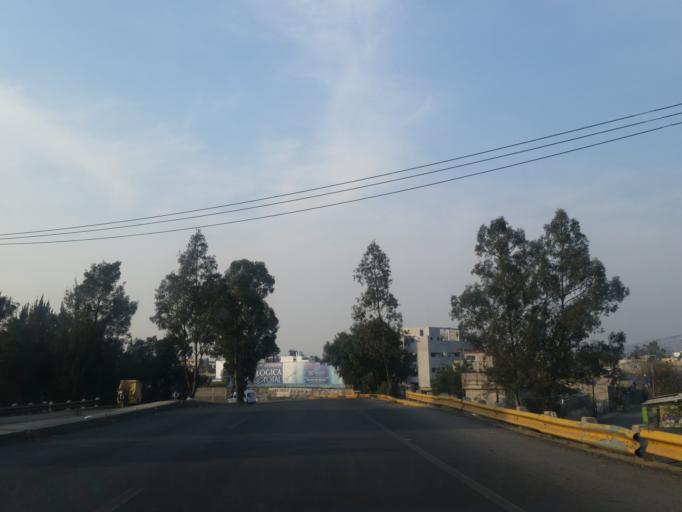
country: MX
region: Mexico
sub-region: La Paz
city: Emiliano Zapata
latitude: 19.3527
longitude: -98.9738
